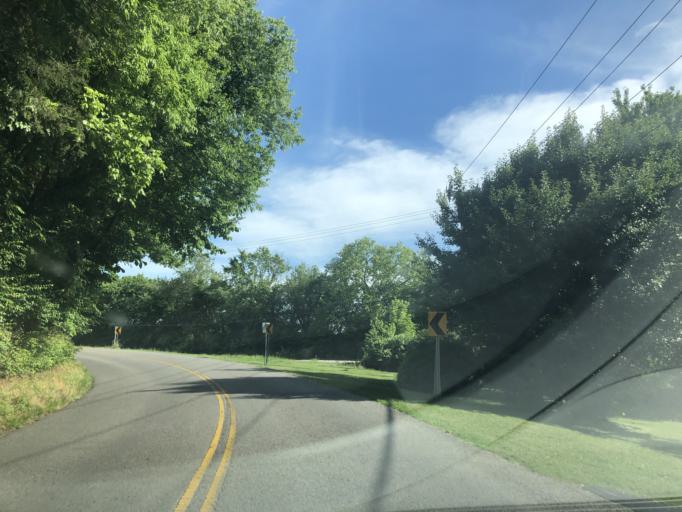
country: US
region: Tennessee
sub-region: Davidson County
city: Belle Meade
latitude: 36.0665
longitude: -86.9418
